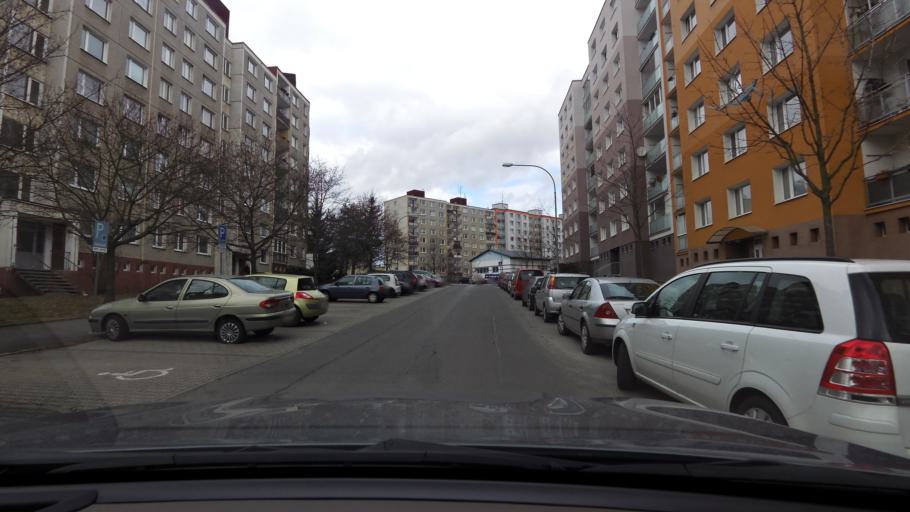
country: CZ
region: Plzensky
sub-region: Okres Plzen-Mesto
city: Pilsen
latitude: 49.7769
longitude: 13.3601
